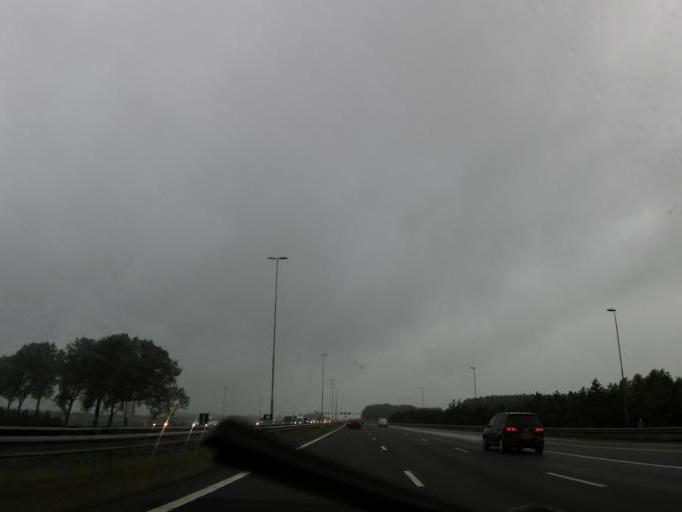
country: NL
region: Gelderland
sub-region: Gemeente Maasdriel
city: Hedel
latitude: 51.7599
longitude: 5.2810
